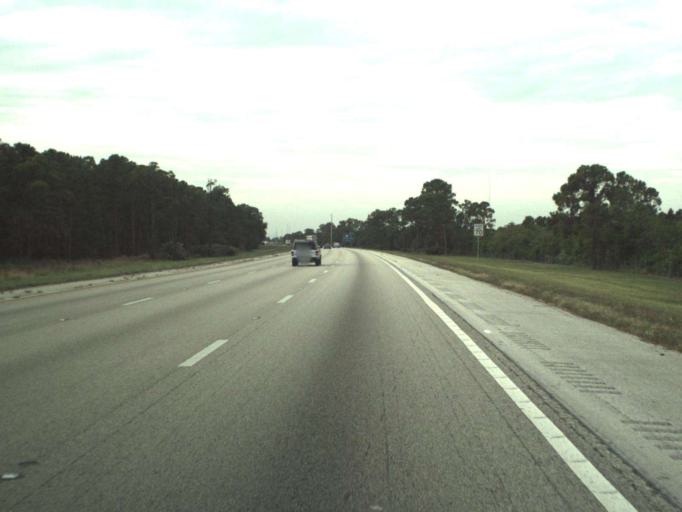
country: US
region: Florida
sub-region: Saint Lucie County
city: Port Saint Lucie
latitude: 27.1768
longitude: -80.3975
